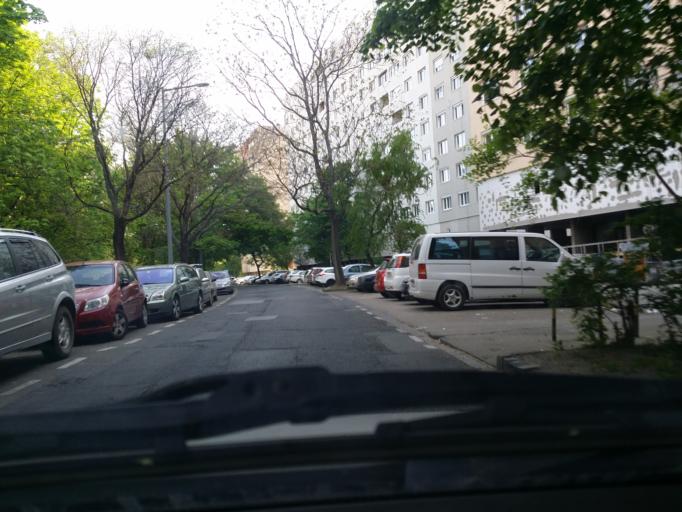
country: HU
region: Budapest
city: Budapest III. keruelet
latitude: 47.5348
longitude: 19.0432
